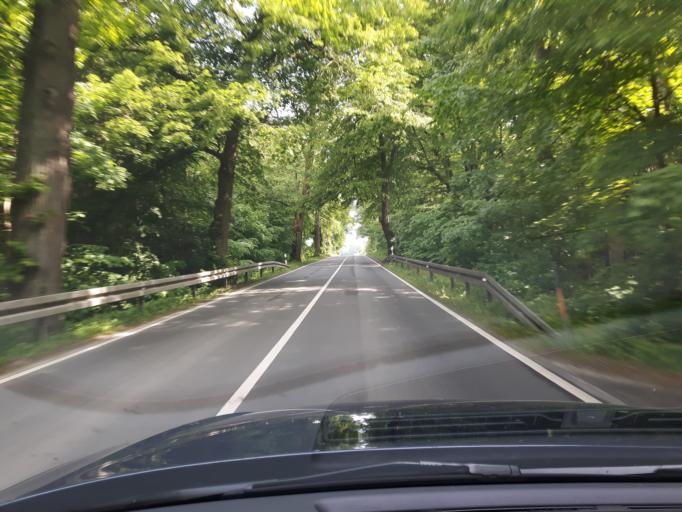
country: DE
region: Mecklenburg-Vorpommern
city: Gross Wokern
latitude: 53.6336
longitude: 12.4758
